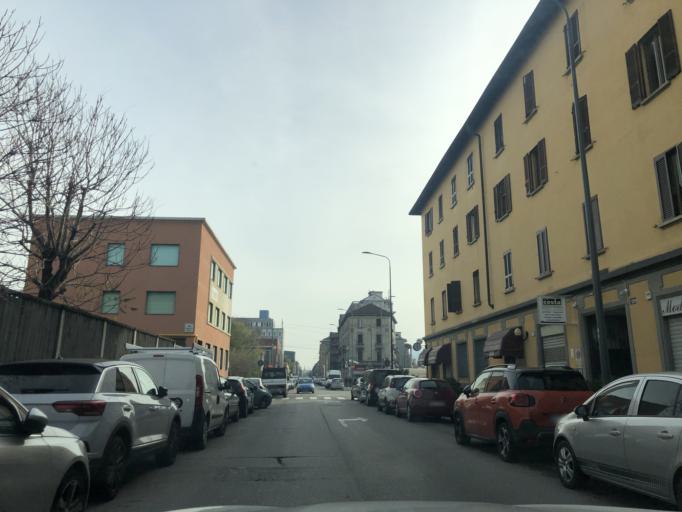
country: IT
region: Lombardy
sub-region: Citta metropolitana di Milano
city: Novate Milanese
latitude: 45.5055
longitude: 9.1365
